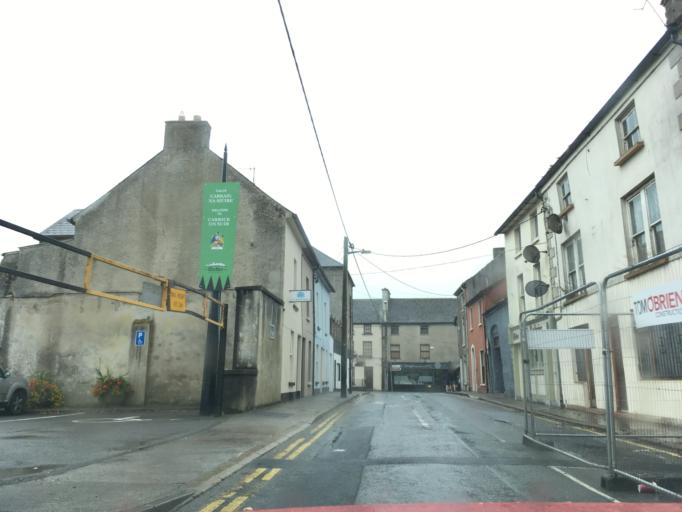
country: IE
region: Munster
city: Carrick-on-Suir
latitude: 52.3458
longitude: -7.4100
